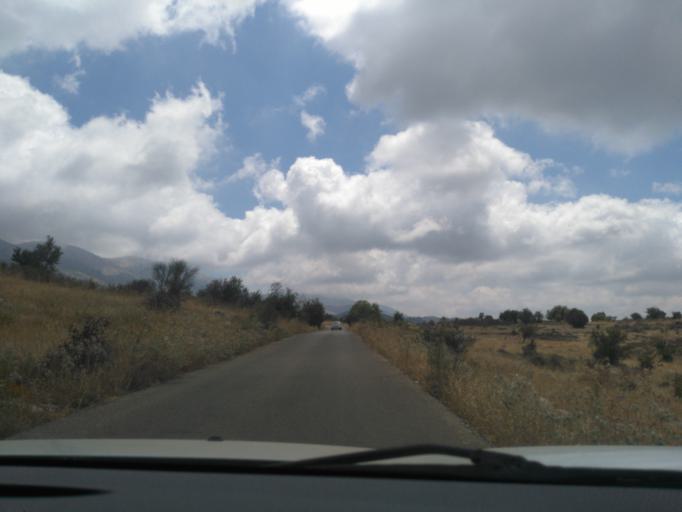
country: LB
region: Mont-Liban
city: Beit ed Dine
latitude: 33.6806
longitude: 35.6638
